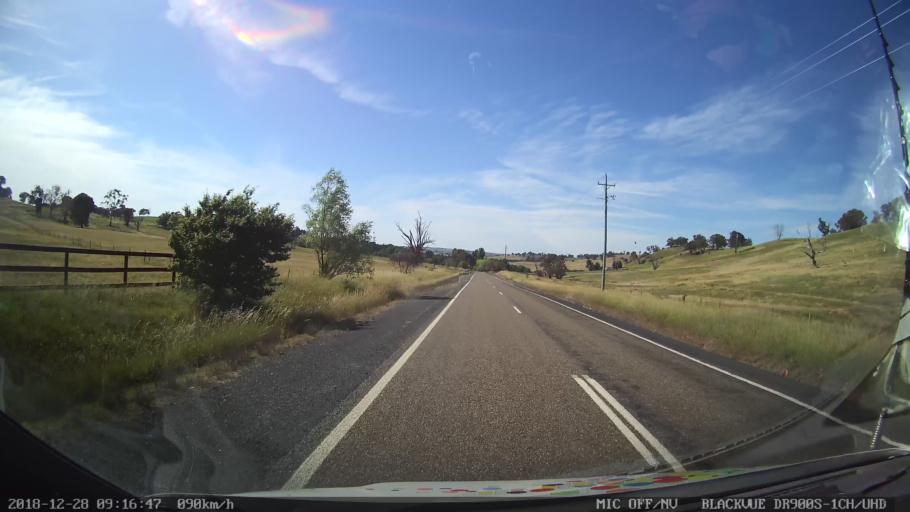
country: AU
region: New South Wales
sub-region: Upper Lachlan Shire
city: Crookwell
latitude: -34.3131
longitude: 149.3571
